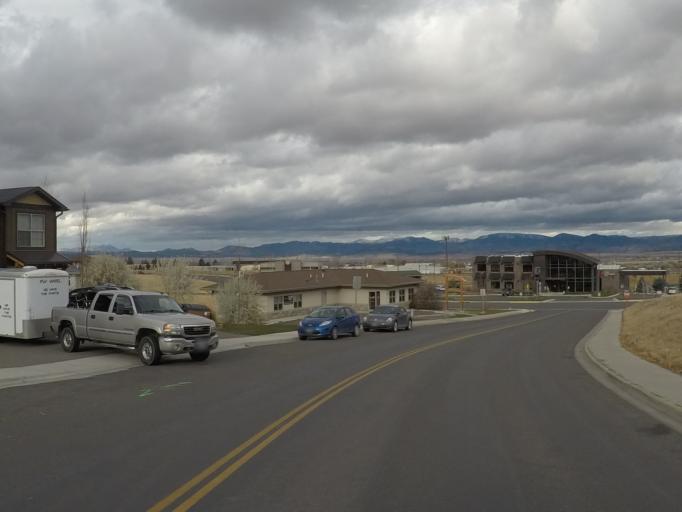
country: US
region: Montana
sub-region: Lewis and Clark County
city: Helena
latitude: 46.5829
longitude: -111.9925
